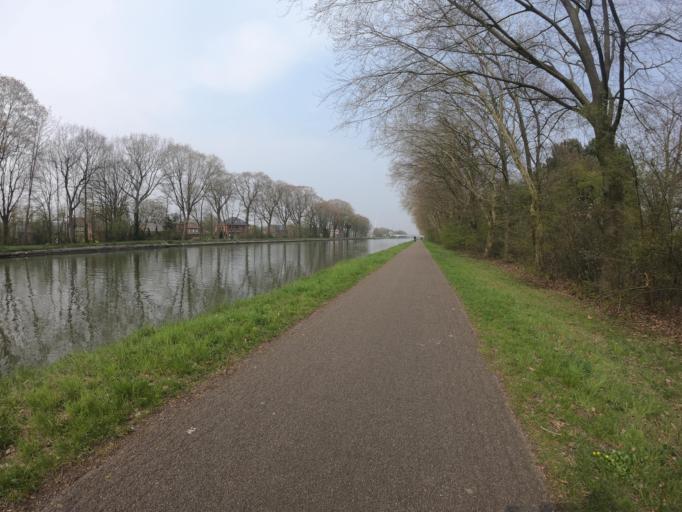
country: BE
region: Flanders
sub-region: Provincie Limburg
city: Maasmechelen
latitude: 51.0334
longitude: 5.7060
